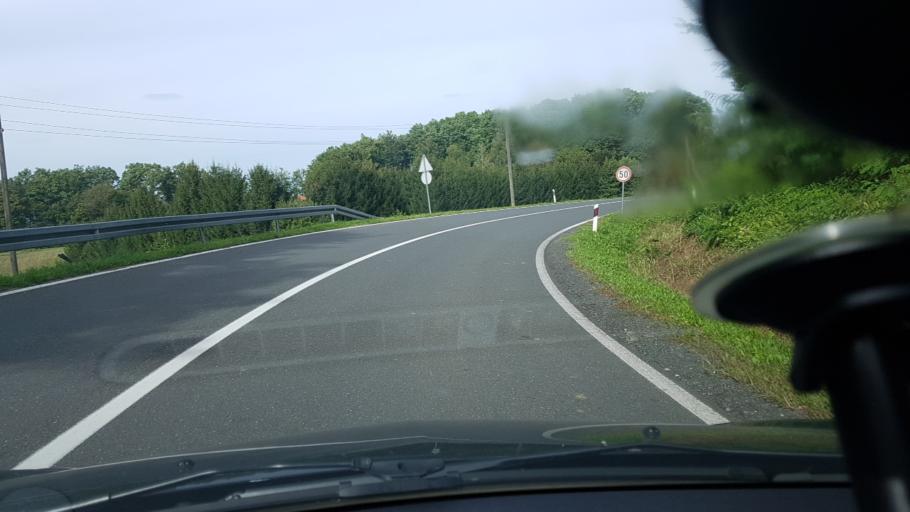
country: HR
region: Varazdinska
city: Ljubescica
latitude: 46.1302
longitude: 16.3607
